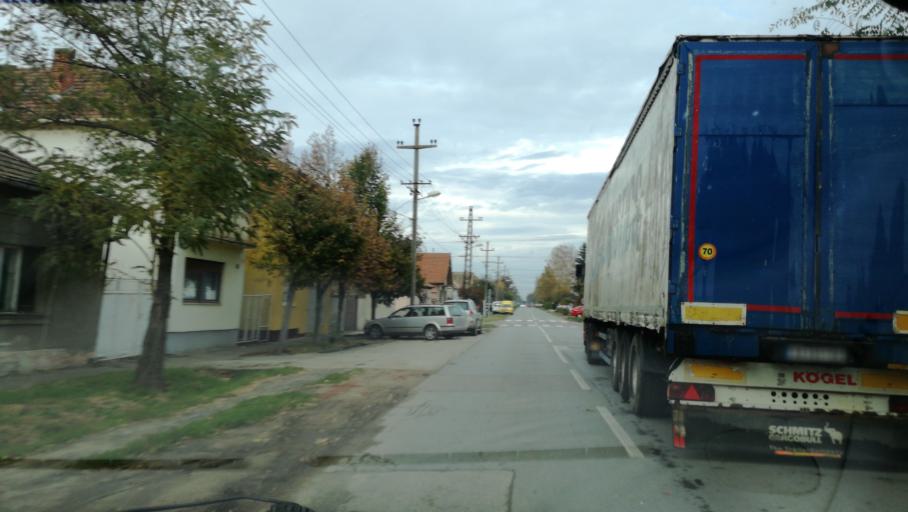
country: RS
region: Autonomna Pokrajina Vojvodina
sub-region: Severnobanatski Okrug
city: Kikinda
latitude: 45.8364
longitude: 20.4710
